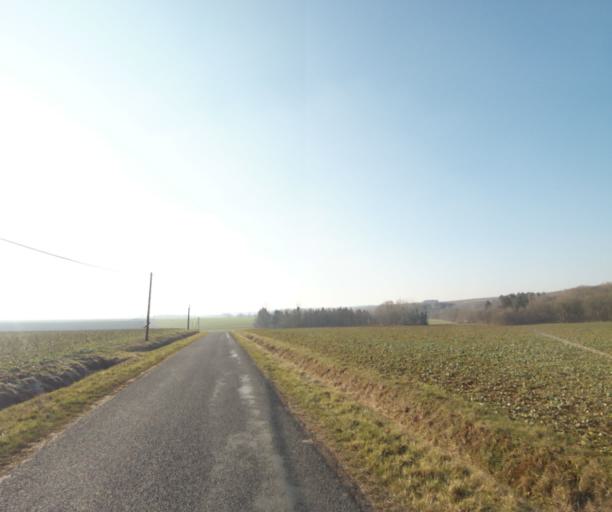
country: FR
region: Champagne-Ardenne
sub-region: Departement de la Haute-Marne
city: Bienville
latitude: 48.5362
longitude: 5.0138
